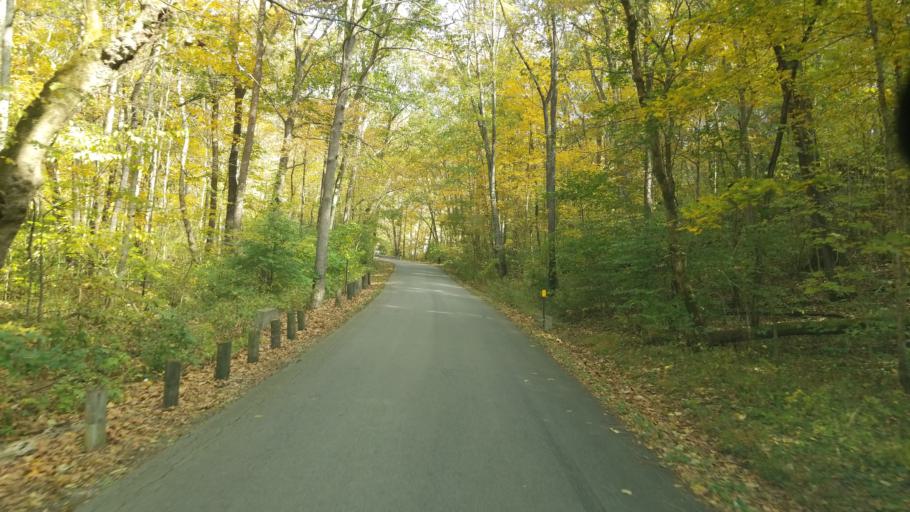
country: US
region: Ohio
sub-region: Warren County
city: Morrow
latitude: 39.3692
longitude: -84.1543
